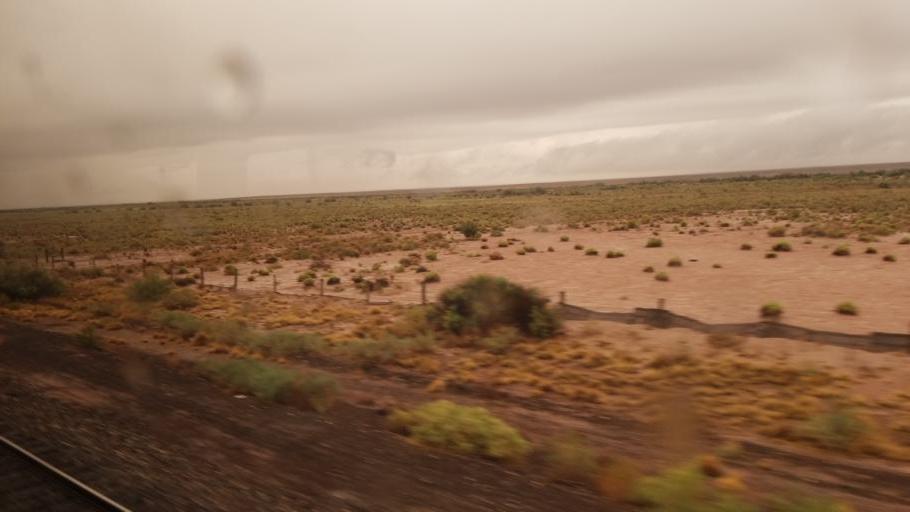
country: US
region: Arizona
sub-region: Navajo County
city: Winslow
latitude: 34.9907
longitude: -110.5877
